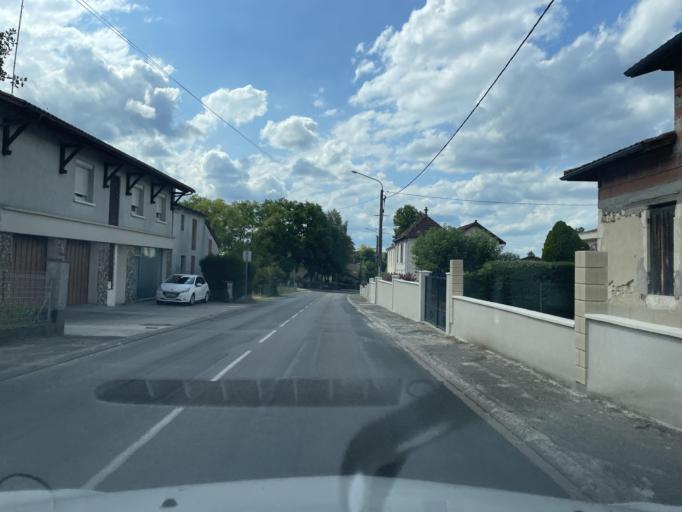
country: FR
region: Aquitaine
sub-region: Departement du Lot-et-Garonne
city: Casteljaloux
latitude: 44.3117
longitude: 0.0957
